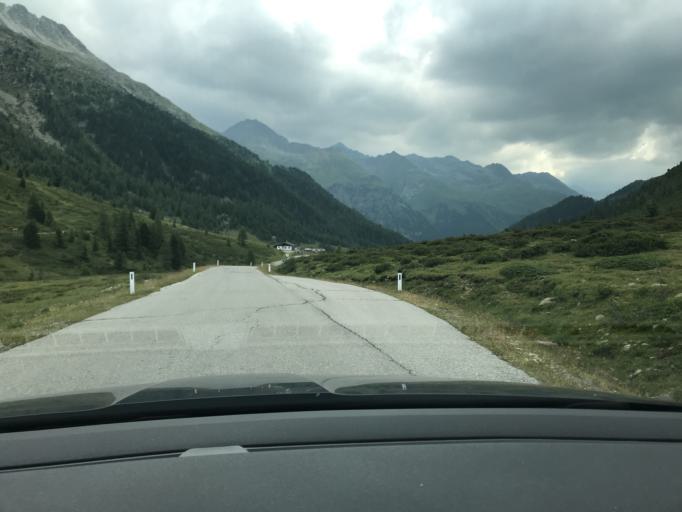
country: IT
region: Trentino-Alto Adige
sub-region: Bolzano
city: San Martino
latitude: 46.8945
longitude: 12.2157
